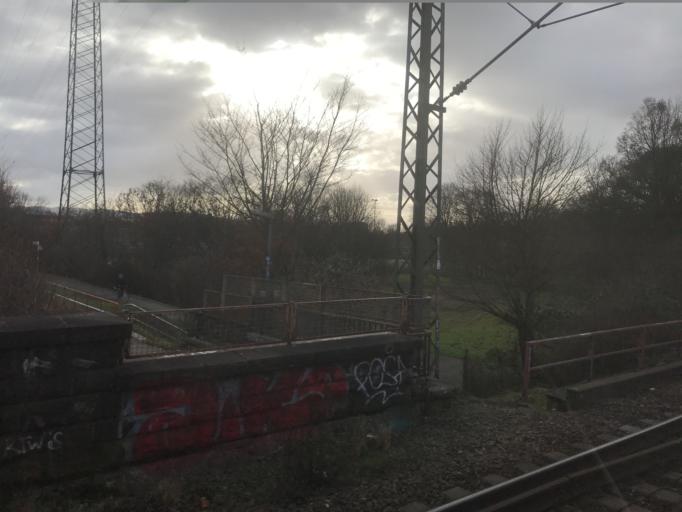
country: DE
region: Baden-Wuerttemberg
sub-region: Freiburg Region
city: Offenburg
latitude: 48.4621
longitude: 7.9375
